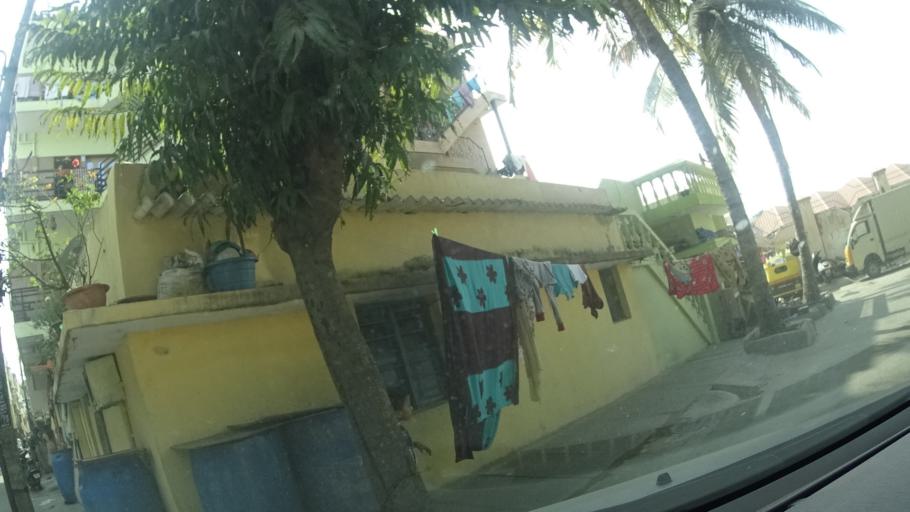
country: IN
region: Karnataka
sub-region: Bangalore Urban
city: Bangalore
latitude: 12.9505
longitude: 77.5552
